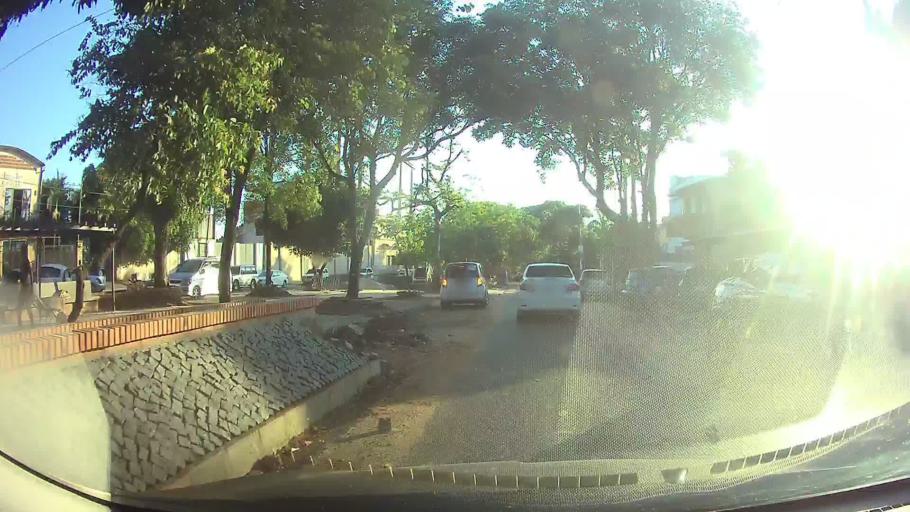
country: PY
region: Asuncion
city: Asuncion
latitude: -25.2972
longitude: -57.6401
